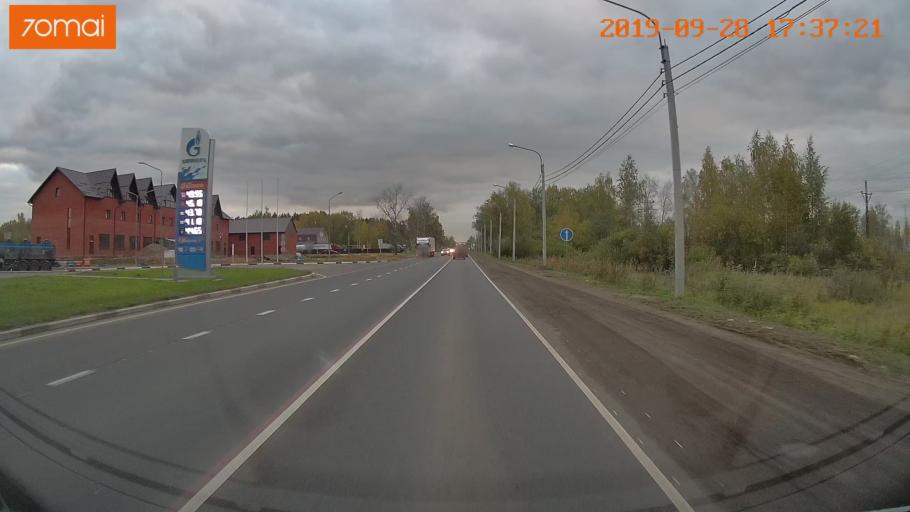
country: RU
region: Jaroslavl
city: Yaroslavl
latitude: 57.5426
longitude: 39.9526
